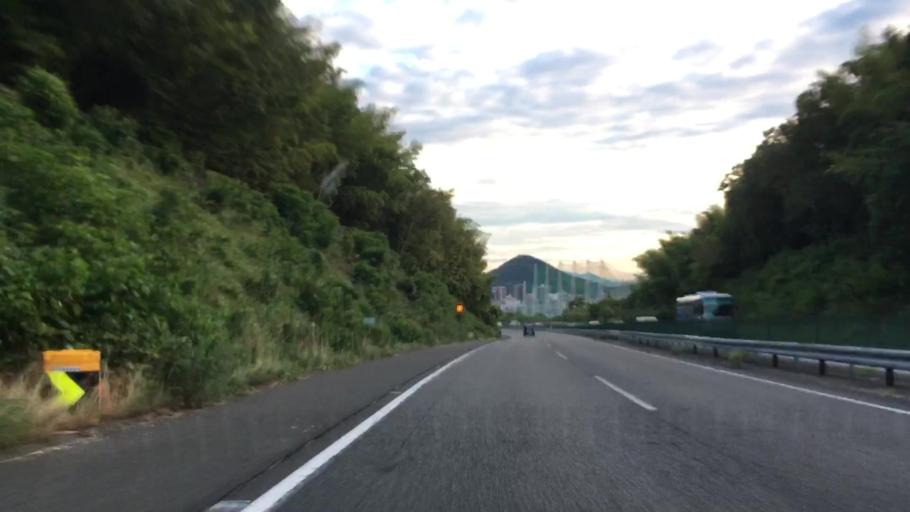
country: JP
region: Yamaguchi
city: Shimonoseki
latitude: 34.0217
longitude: 130.9597
